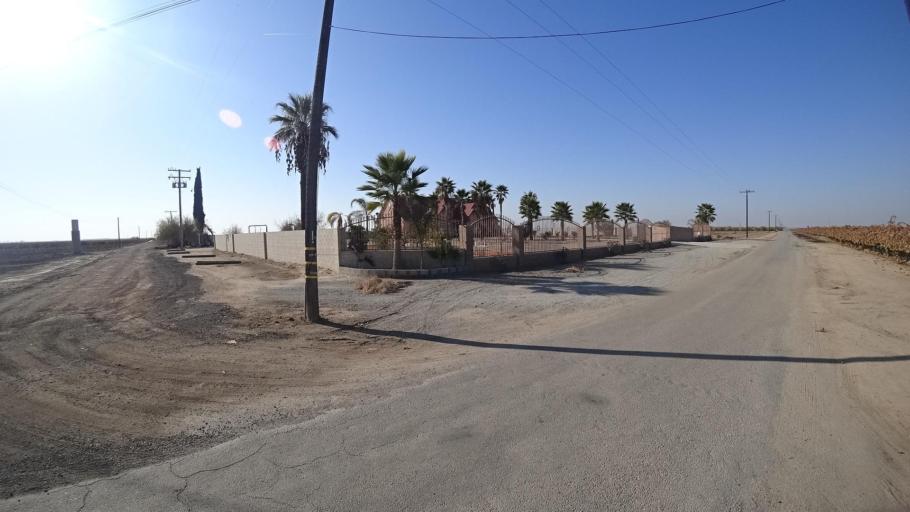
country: US
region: California
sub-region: Kern County
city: Delano
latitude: 35.7397
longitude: -119.2143
